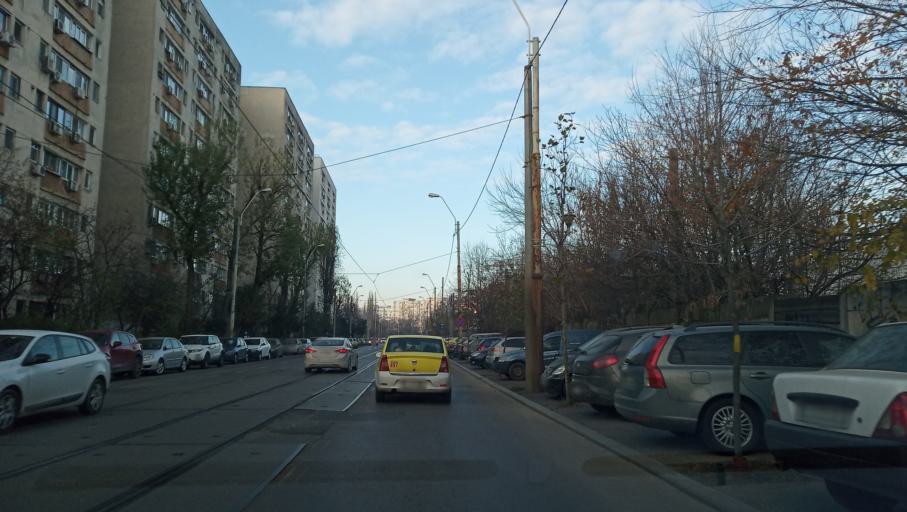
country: RO
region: Ilfov
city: Dobroesti
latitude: 44.4312
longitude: 26.1732
